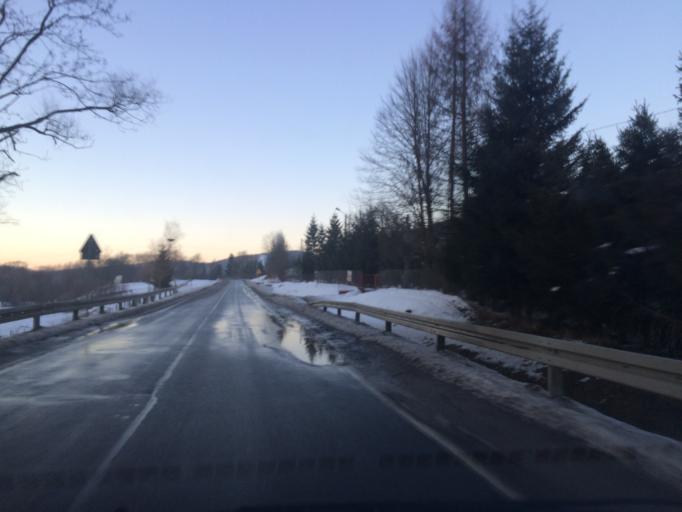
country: PL
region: Subcarpathian Voivodeship
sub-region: Powiat bieszczadzki
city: Czarna
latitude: 49.3747
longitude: 22.6458
